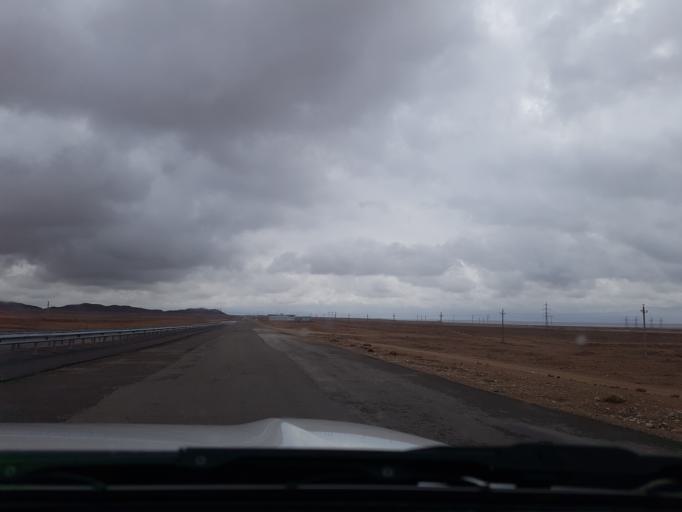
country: TM
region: Balkan
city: Balkanabat
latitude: 39.9339
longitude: 53.8602
